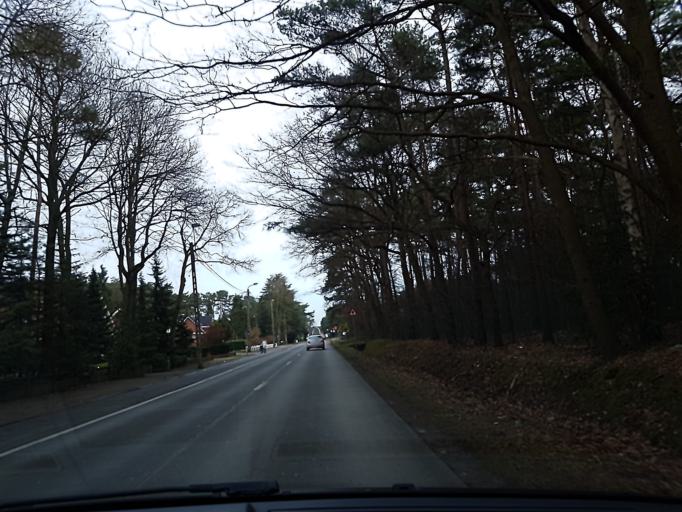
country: BE
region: Flanders
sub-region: Provincie Vlaams-Brabant
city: Boortmeerbeek
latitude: 51.0085
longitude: 4.5947
